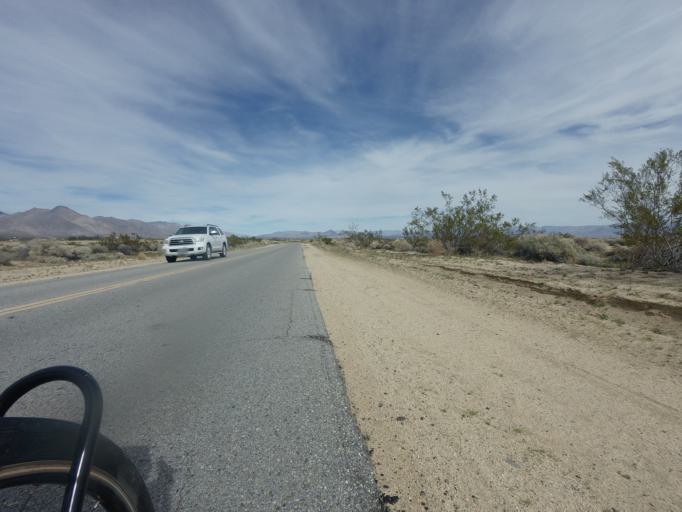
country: US
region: California
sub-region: Kern County
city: Inyokern
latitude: 35.7169
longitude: -117.8333
